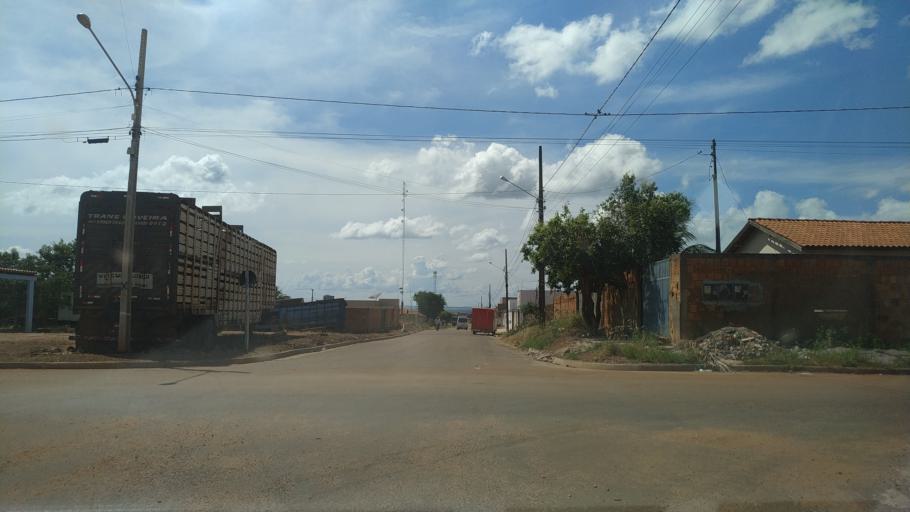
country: BR
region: Mato Grosso
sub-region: Pontes E Lacerda
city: Pontes e Lacerda
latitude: -15.2504
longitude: -59.3174
